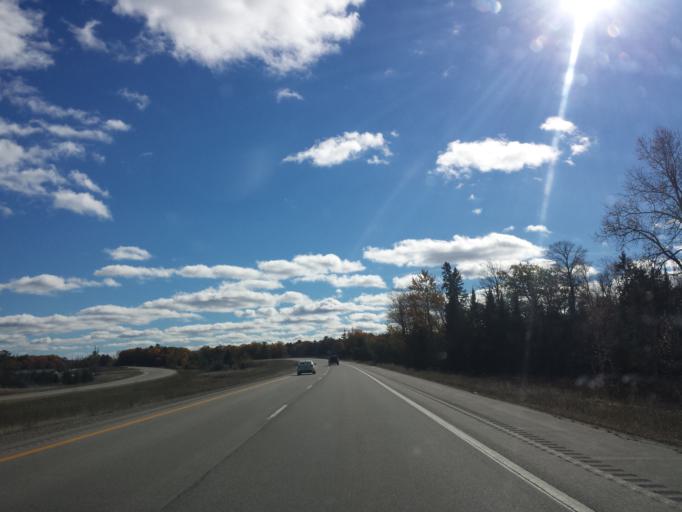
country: US
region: Michigan
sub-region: Cheboygan County
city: Indian River
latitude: 45.4576
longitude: -84.6153
